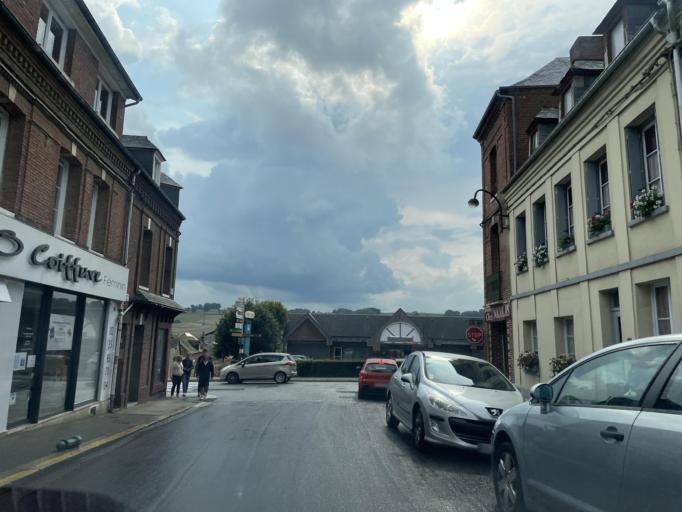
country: FR
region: Haute-Normandie
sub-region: Departement de la Seine-Maritime
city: Envermeu
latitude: 49.8962
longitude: 1.2643
